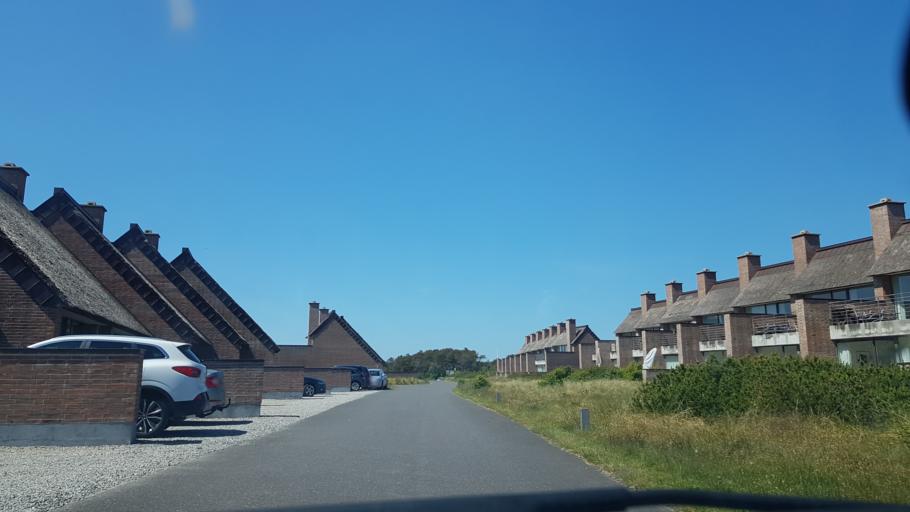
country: DE
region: Schleswig-Holstein
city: List
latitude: 55.0861
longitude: 8.5546
